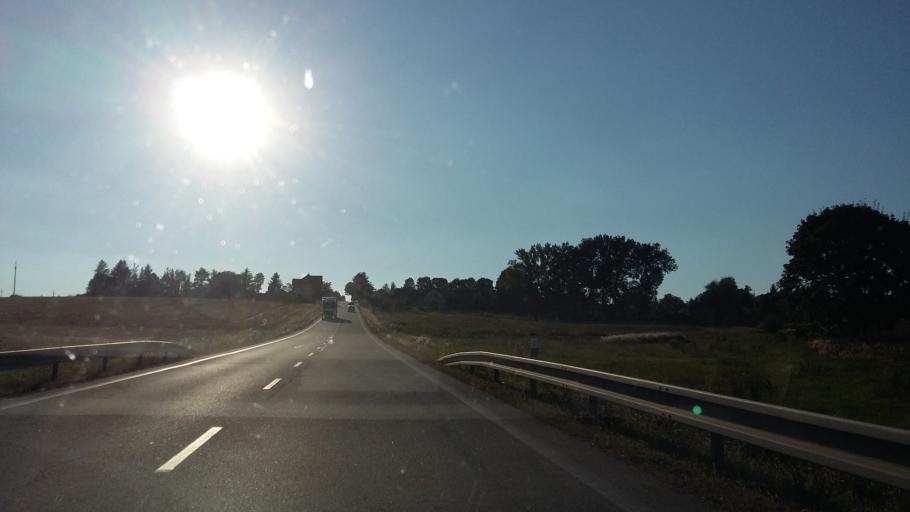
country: CZ
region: Vysocina
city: Velky Beranov
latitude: 49.4012
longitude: 15.6775
